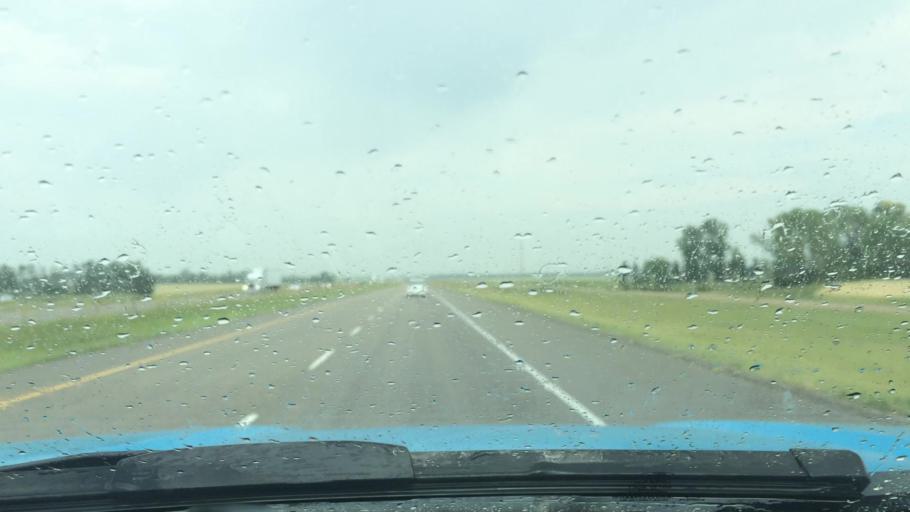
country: CA
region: Alberta
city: Olds
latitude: 51.7198
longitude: -114.0255
